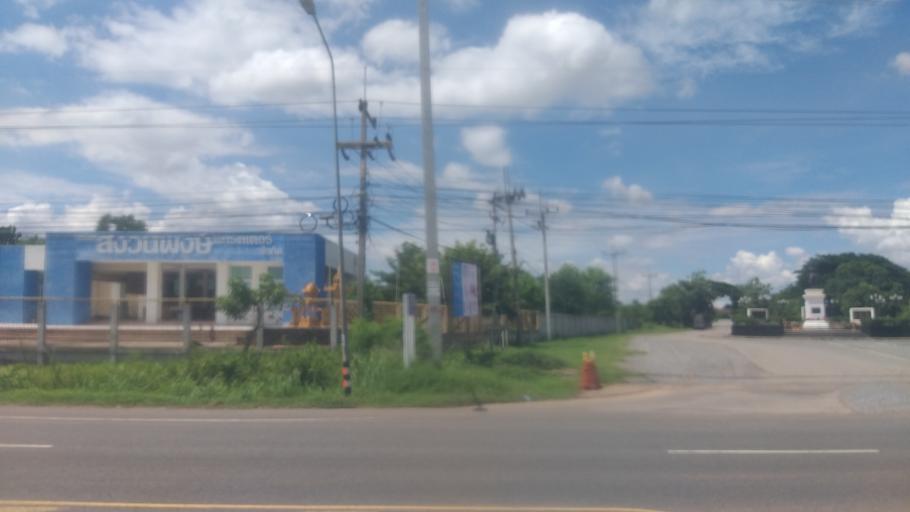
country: TH
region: Nakhon Ratchasima
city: Phra Thong Kham
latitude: 15.3033
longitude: 101.9761
